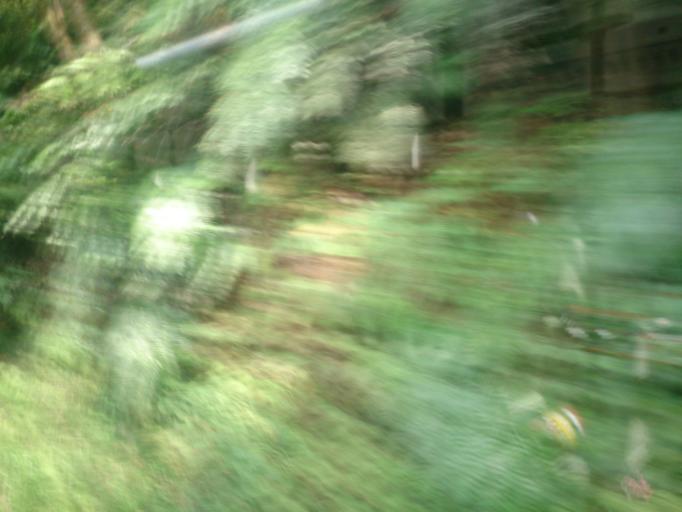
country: TW
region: Taipei
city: Taipei
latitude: 25.1712
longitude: 121.5407
